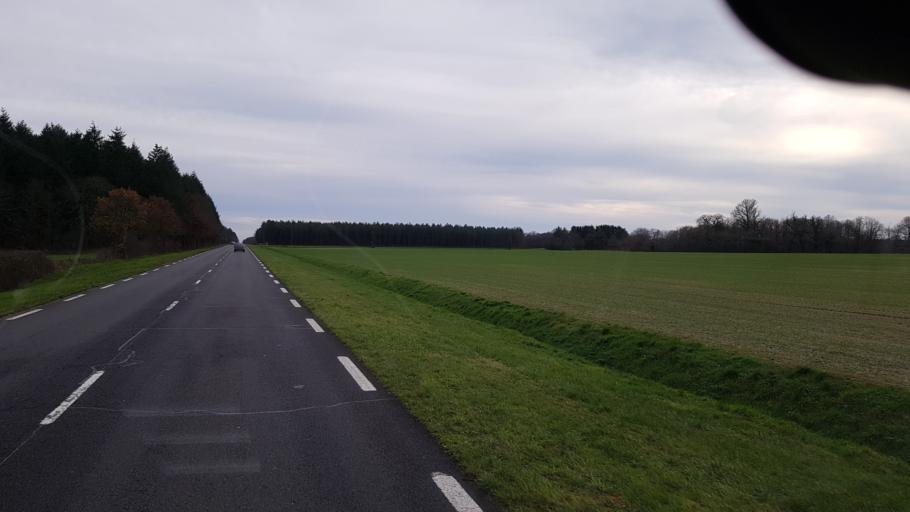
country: FR
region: Centre
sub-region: Departement du Loir-et-Cher
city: Lamotte-Beuvron
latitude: 47.6395
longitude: 1.9978
